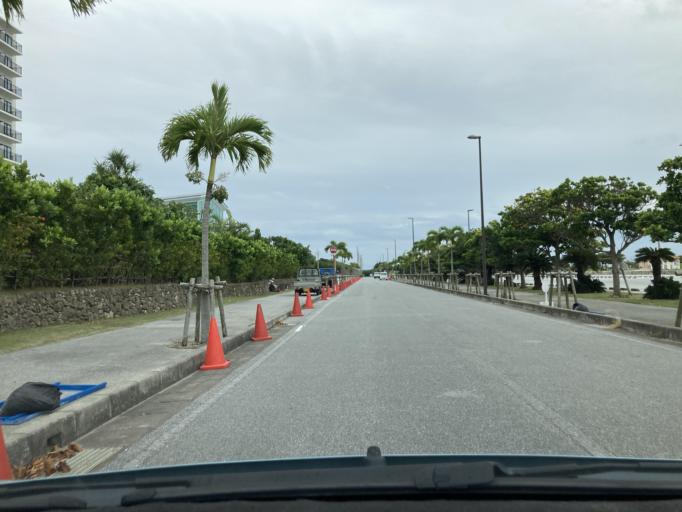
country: JP
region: Okinawa
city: Itoman
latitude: 26.1320
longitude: 127.6523
